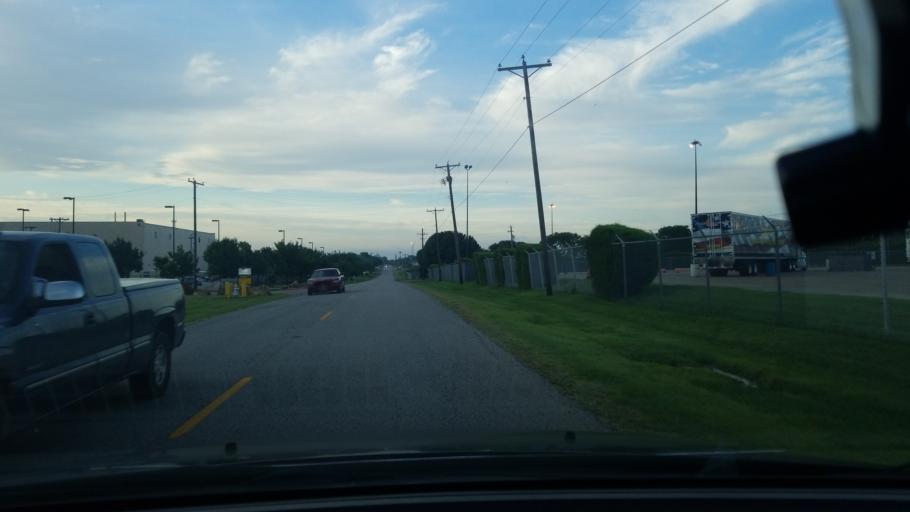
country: US
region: Texas
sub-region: Dallas County
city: Balch Springs
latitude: 32.7724
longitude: -96.6549
